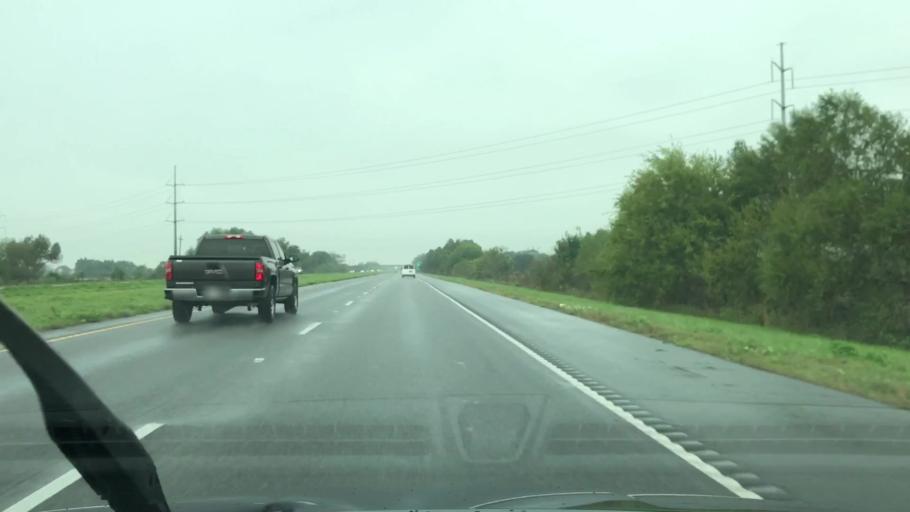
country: US
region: Louisiana
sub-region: Lafourche Parish
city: Raceland
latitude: 29.6900
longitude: -90.6111
